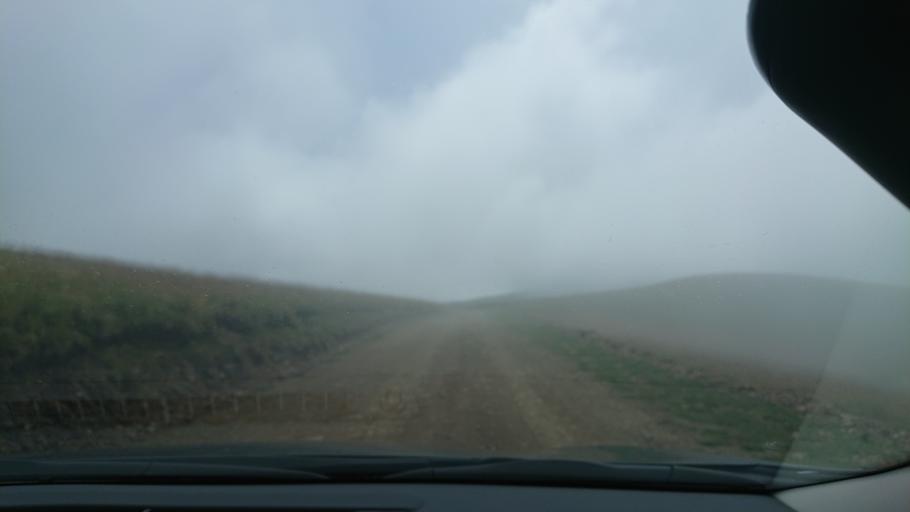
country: TR
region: Gumushane
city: Kurtun
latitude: 40.6324
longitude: 38.9977
